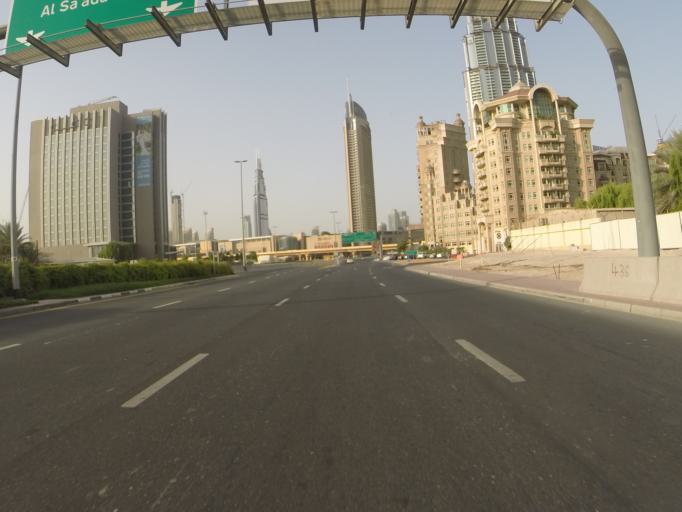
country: AE
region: Dubai
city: Dubai
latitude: 25.2046
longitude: 55.2787
